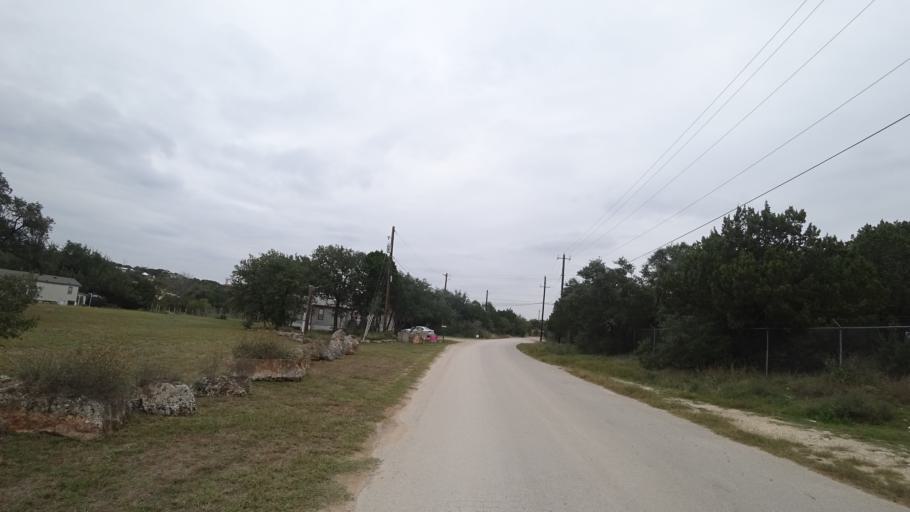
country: US
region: Texas
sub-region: Travis County
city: Hudson Bend
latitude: 30.3836
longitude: -97.9376
